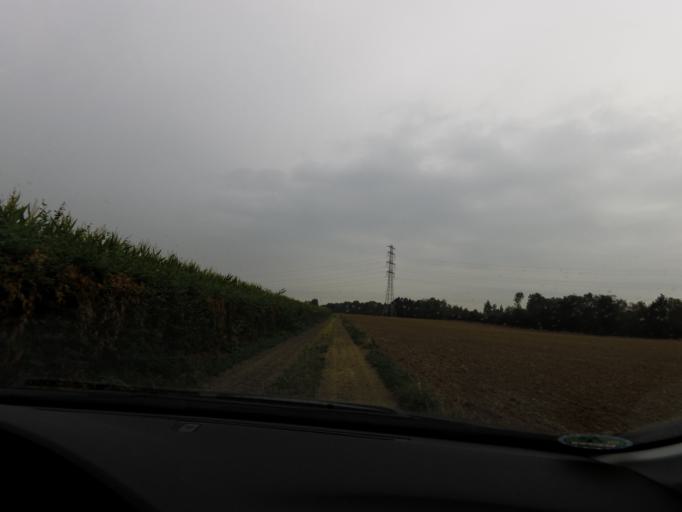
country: NL
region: Limburg
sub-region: Gemeente Simpelveld
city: Simpelveld
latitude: 50.8499
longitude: 5.9757
